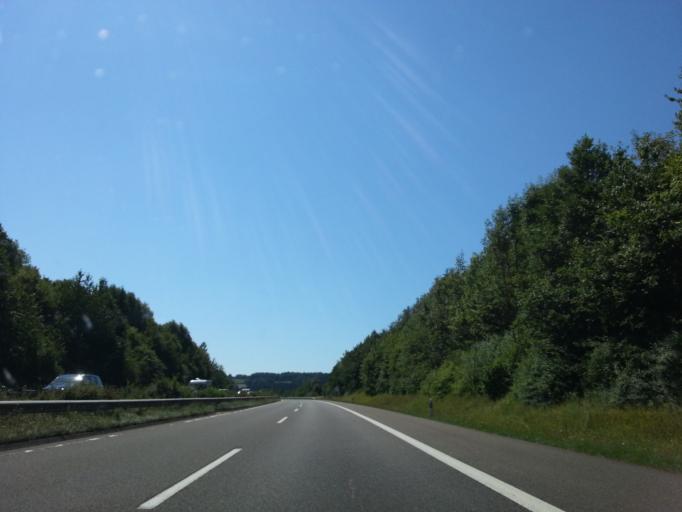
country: DE
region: Rheinland-Pfalz
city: Winringen
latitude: 50.1433
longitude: 6.4049
